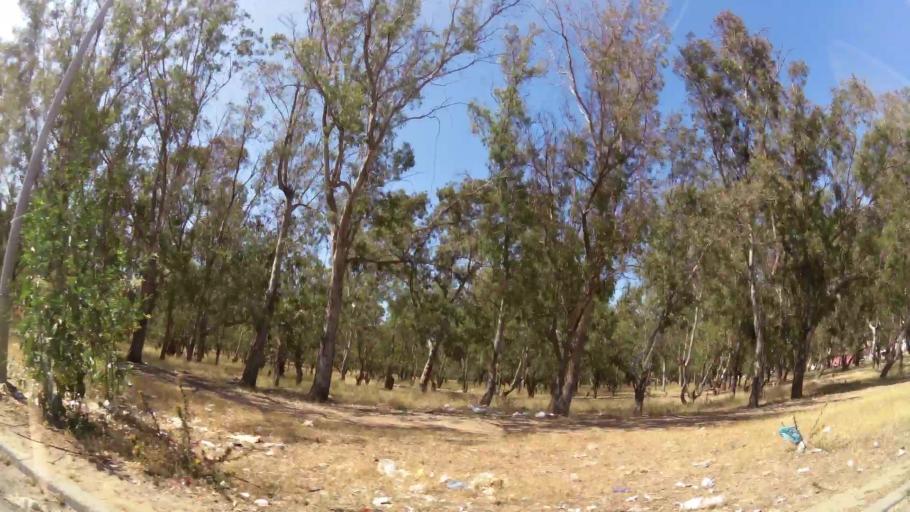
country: MA
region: Gharb-Chrarda-Beni Hssen
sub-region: Kenitra Province
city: Kenitra
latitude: 34.2371
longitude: -6.5588
